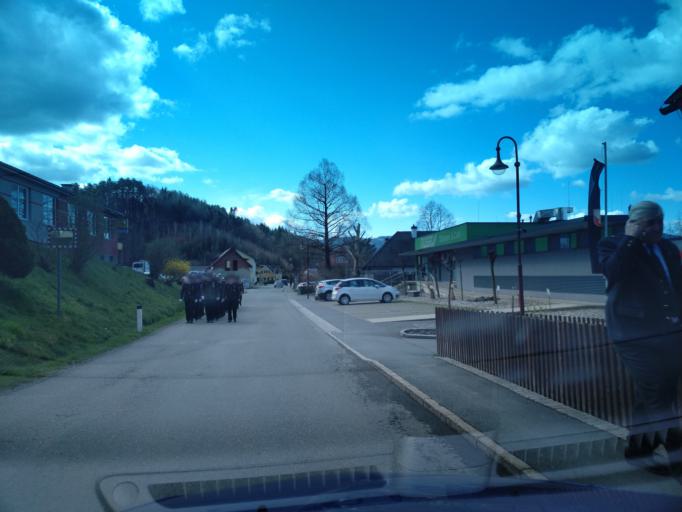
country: AT
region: Styria
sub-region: Politischer Bezirk Leibnitz
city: Sankt Johann im Saggautal
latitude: 46.7011
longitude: 15.4006
